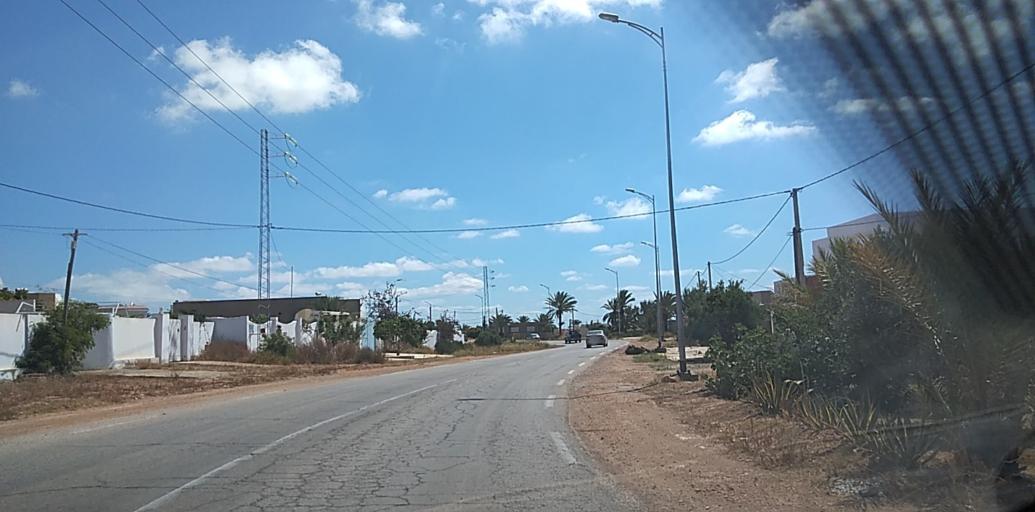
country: TN
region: Safaqis
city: Al Qarmadah
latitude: 34.6766
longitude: 11.1497
